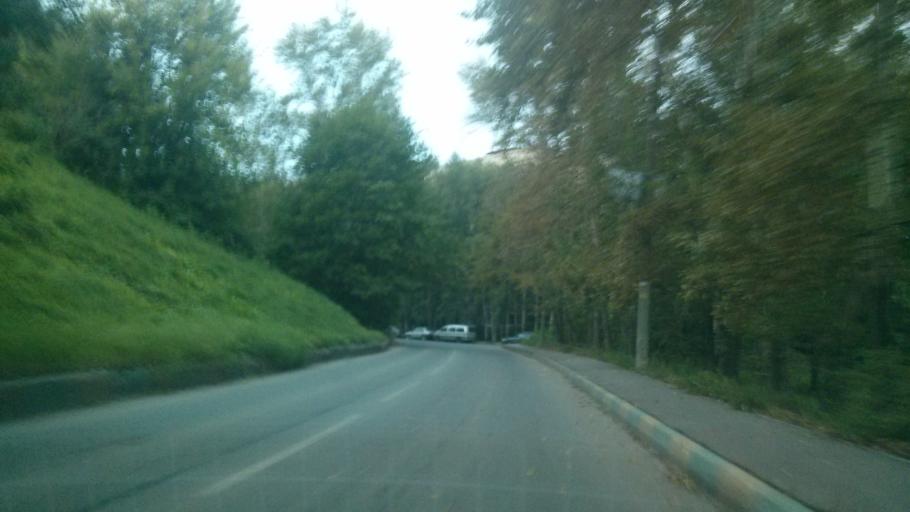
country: RU
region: Nizjnij Novgorod
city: Afonino
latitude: 56.2993
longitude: 44.0690
